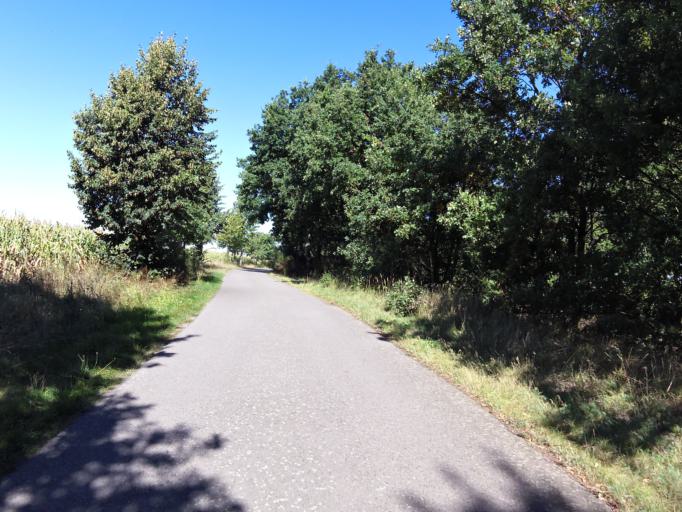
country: DE
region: Saxony
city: Dommitzsch
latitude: 51.6668
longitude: 12.8346
